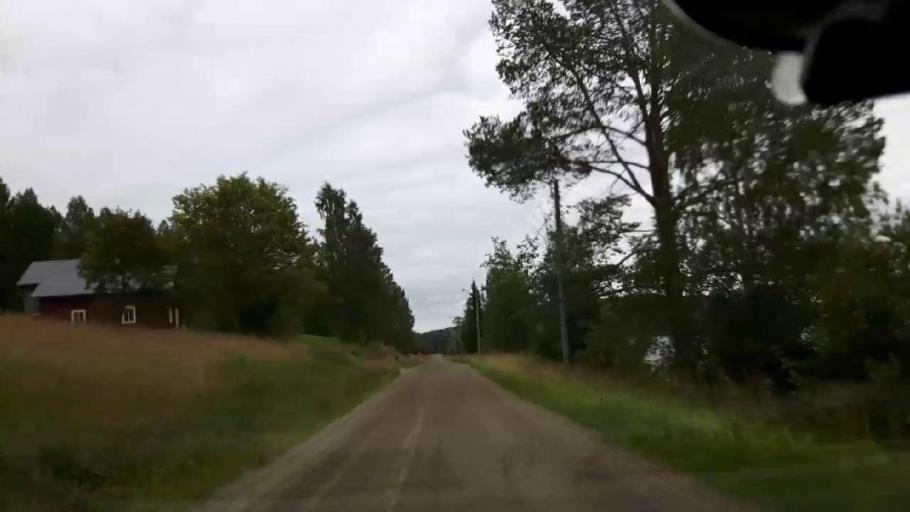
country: SE
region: Jaemtland
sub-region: Braecke Kommun
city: Braecke
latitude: 62.9982
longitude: 15.3815
